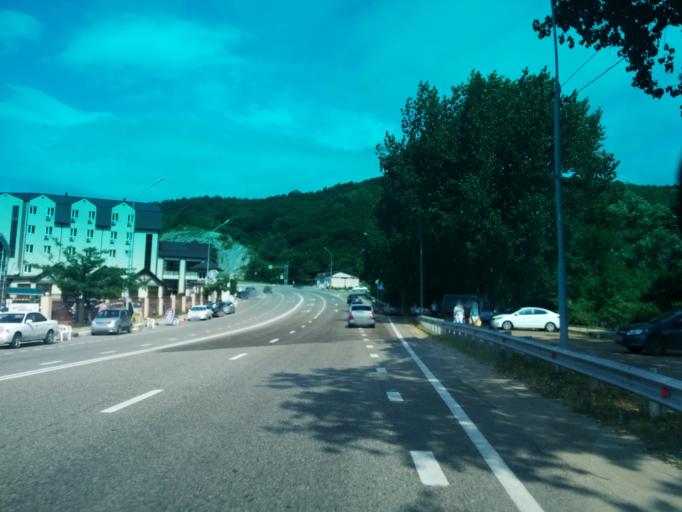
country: RU
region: Krasnodarskiy
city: Nebug
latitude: 44.1655
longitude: 39.0001
